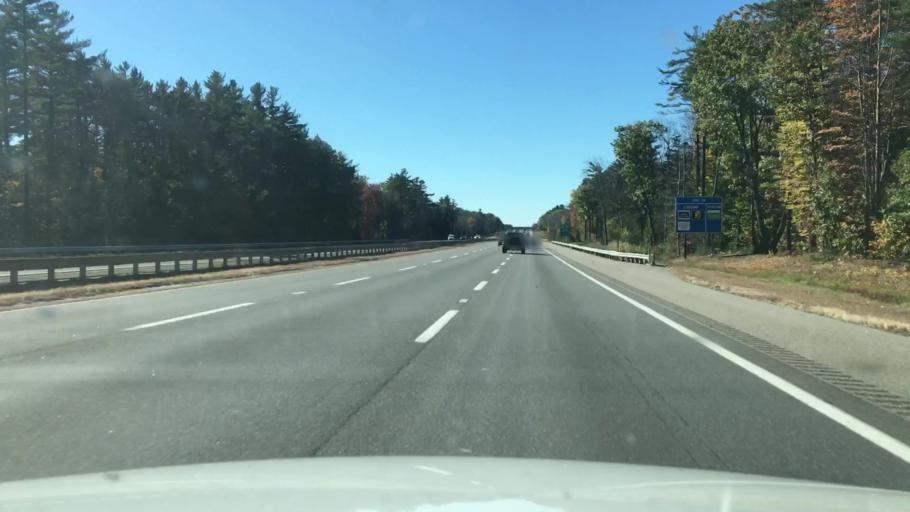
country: US
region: Maine
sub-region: York County
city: Wells Beach Station
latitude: 43.3456
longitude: -70.5959
